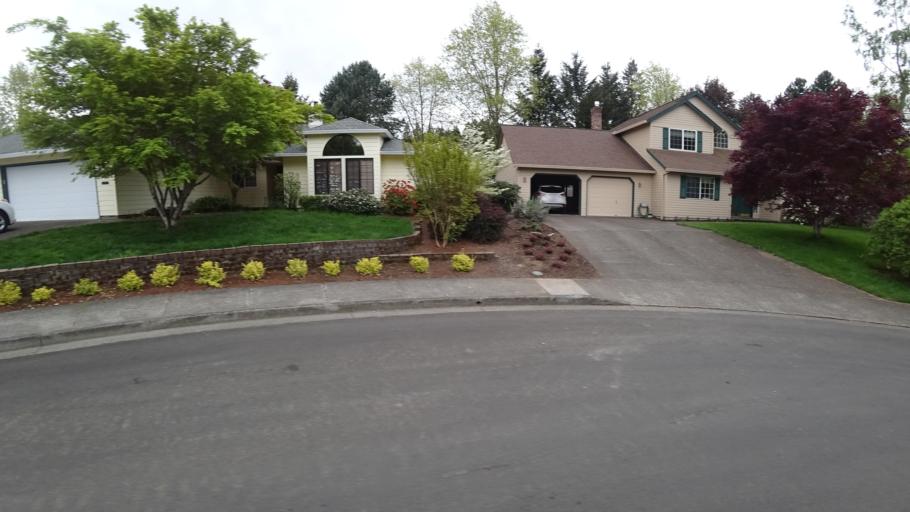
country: US
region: Oregon
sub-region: Washington County
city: Hillsboro
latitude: 45.5400
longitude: -122.9888
